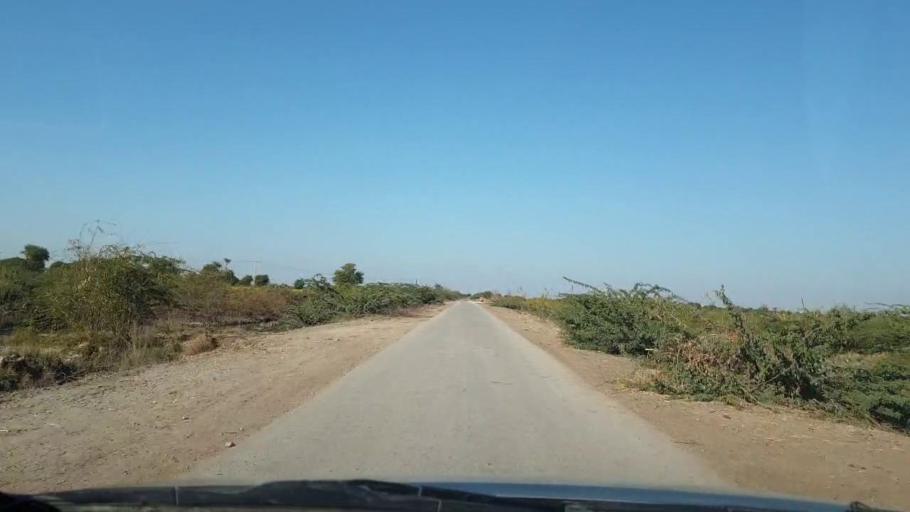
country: PK
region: Sindh
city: Jhol
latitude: 25.8410
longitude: 68.9513
